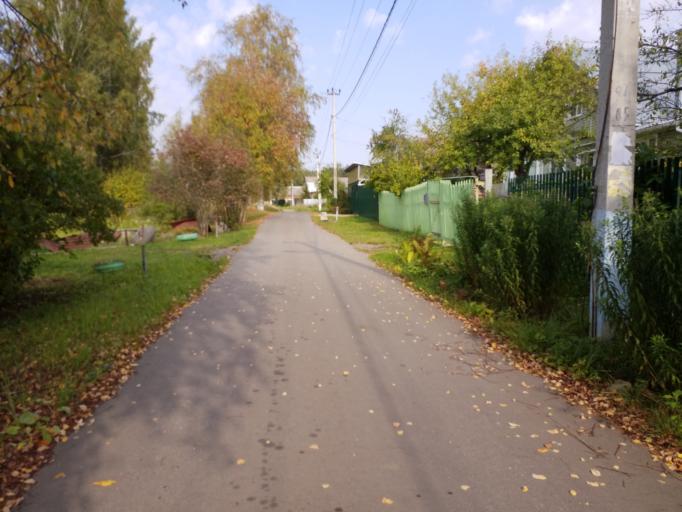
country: RU
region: Moskovskaya
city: Ashukino
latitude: 56.1654
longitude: 37.9642
